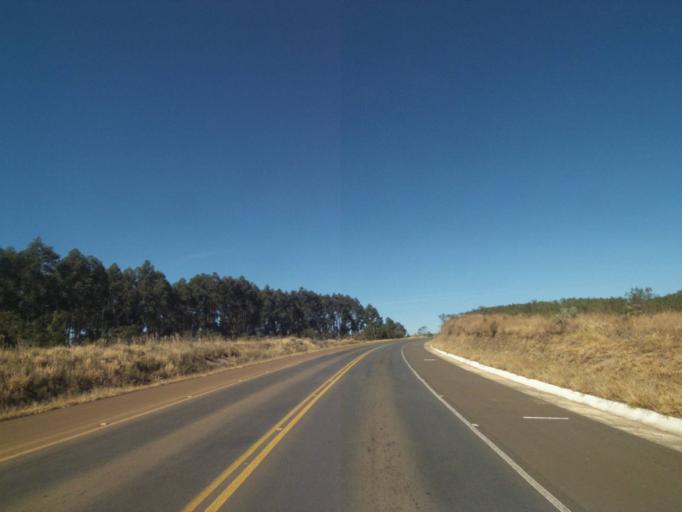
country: BR
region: Parana
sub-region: Tibagi
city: Tibagi
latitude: -24.6881
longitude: -50.4402
